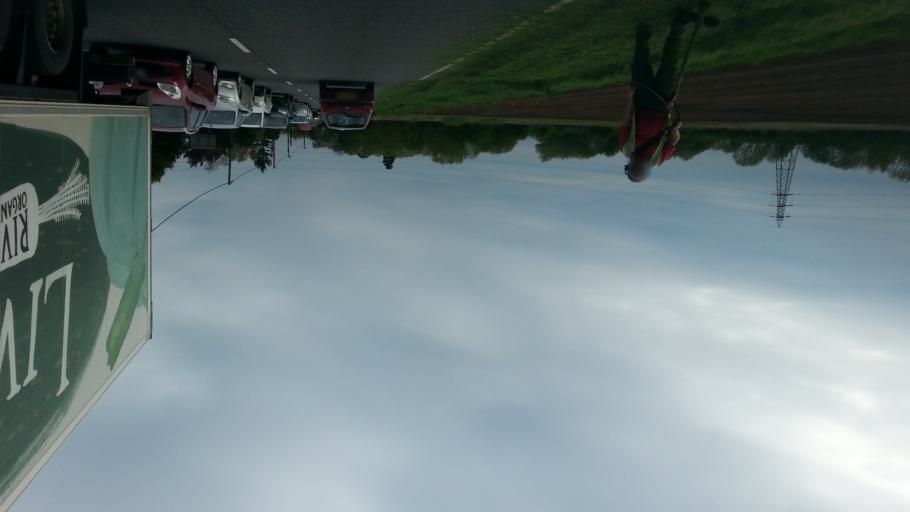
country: GB
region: England
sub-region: Cambridgeshire
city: March
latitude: 52.5720
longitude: 0.0584
